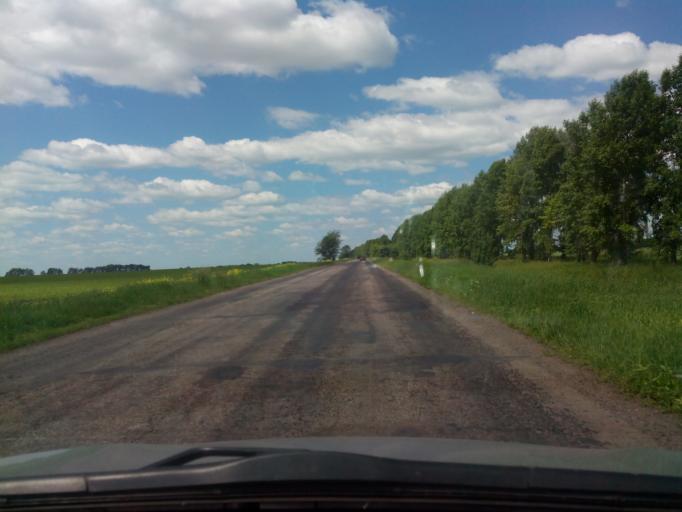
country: RU
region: Voronezj
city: Gribanovskiy
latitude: 51.6216
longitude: 41.9548
